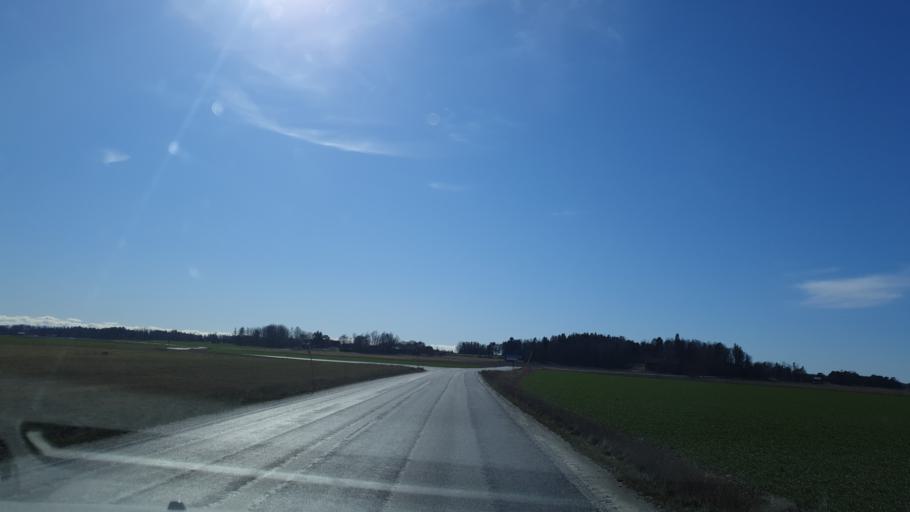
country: SE
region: Uppsala
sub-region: Enkopings Kommun
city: Grillby
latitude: 59.6036
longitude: 17.2733
